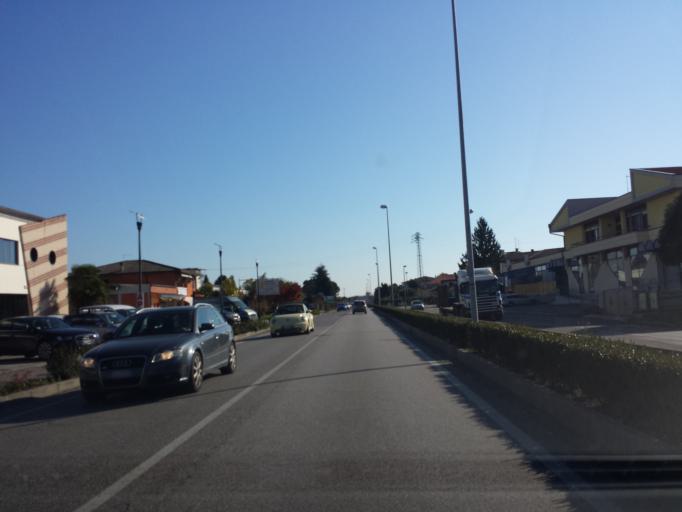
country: IT
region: Veneto
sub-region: Provincia di Vicenza
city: Camisano Vicentino
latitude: 45.5200
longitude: 11.6934
